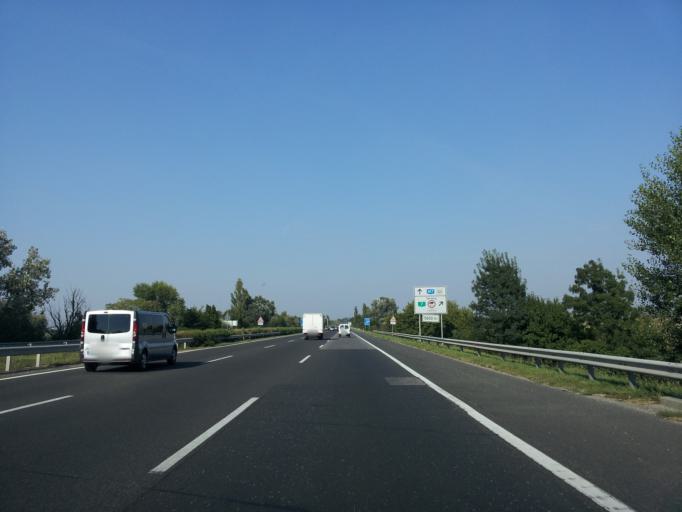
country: HU
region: Fejer
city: Szekesfehervar
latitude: 47.1564
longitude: 18.4467
